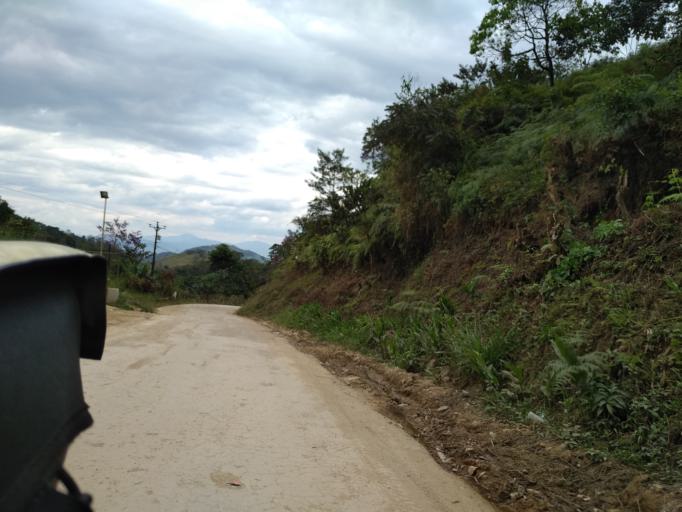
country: PE
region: Cajamarca
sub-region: Provincia de San Ignacio
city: Namballe
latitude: -4.8614
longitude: -79.1263
